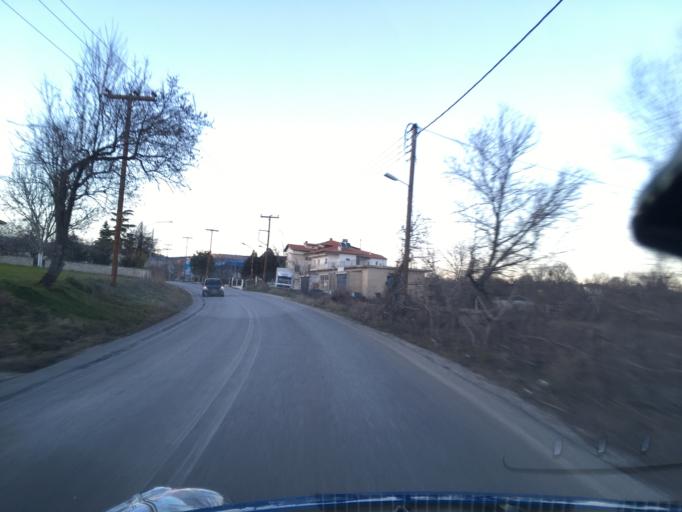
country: GR
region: West Macedonia
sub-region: Nomos Kozanis
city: Kozani
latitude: 40.2802
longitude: 21.7834
